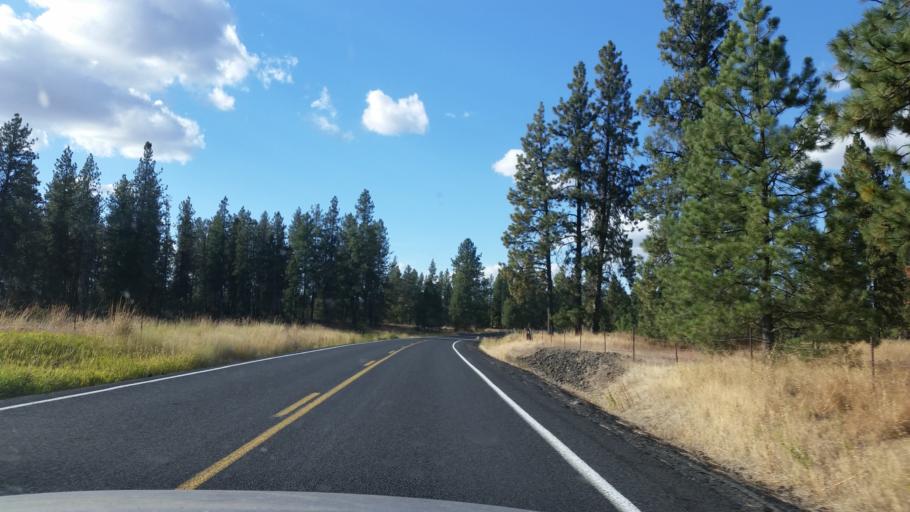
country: US
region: Washington
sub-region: Spokane County
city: Cheney
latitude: 47.4400
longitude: -117.5739
